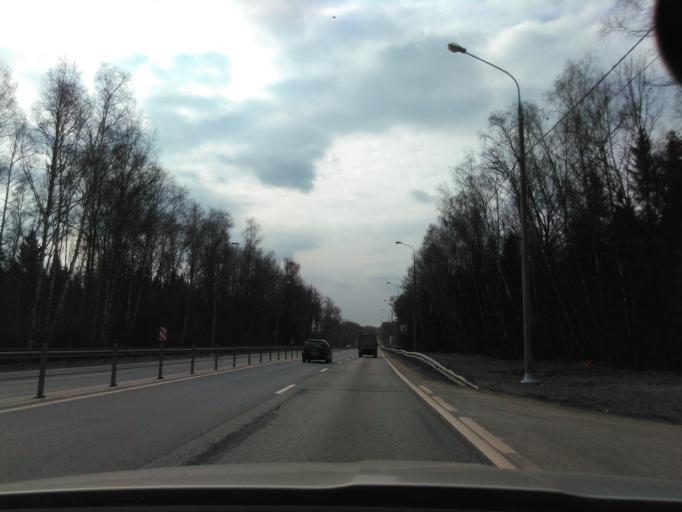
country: RU
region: Moskovskaya
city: Marfino
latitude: 56.0236
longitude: 37.5438
